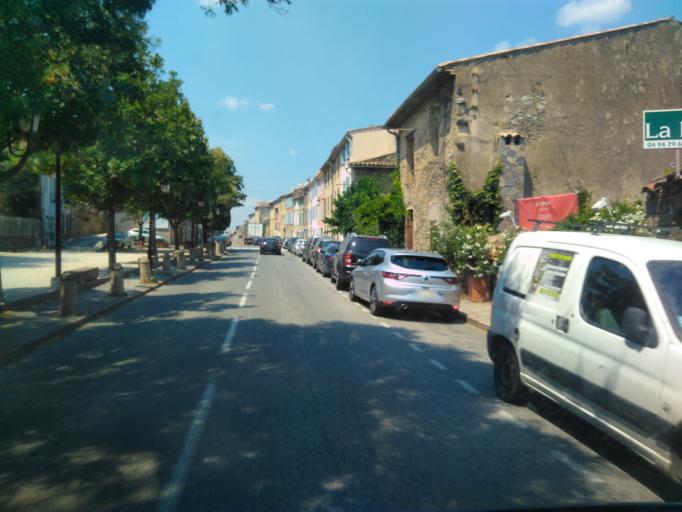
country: FR
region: Provence-Alpes-Cote d'Azur
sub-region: Departement du Var
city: La Garde-Freinet
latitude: 43.3153
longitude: 6.4709
